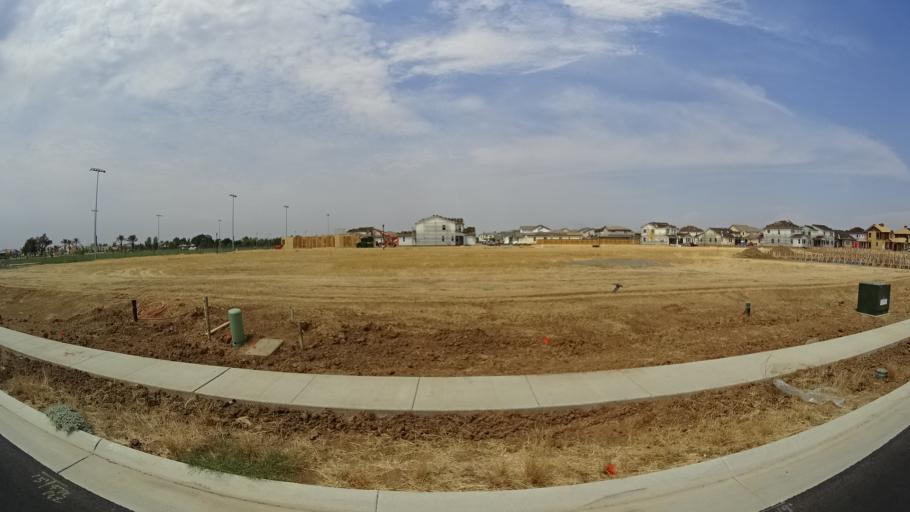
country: US
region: California
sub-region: Sacramento County
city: Laguna
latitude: 38.3907
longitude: -121.4066
